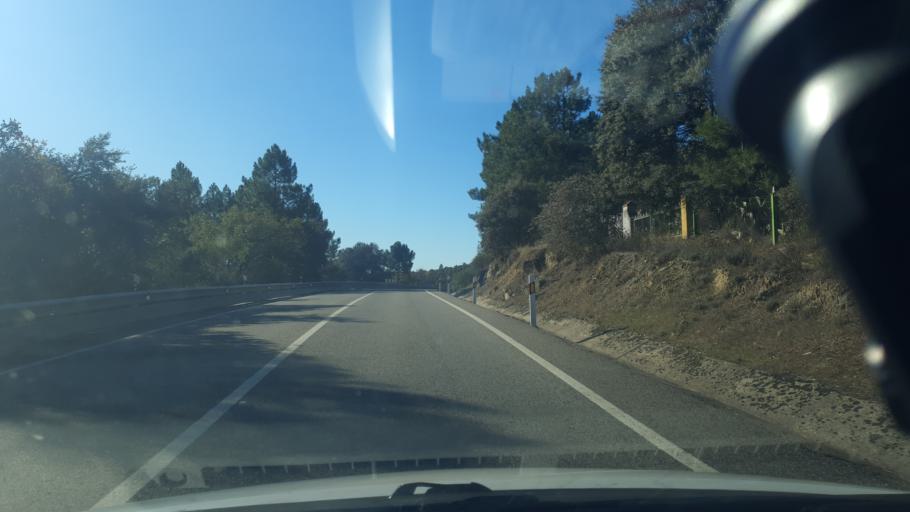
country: ES
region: Castille and Leon
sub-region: Provincia de Avila
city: Arenas de San Pedro
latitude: 40.1972
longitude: -5.0453
